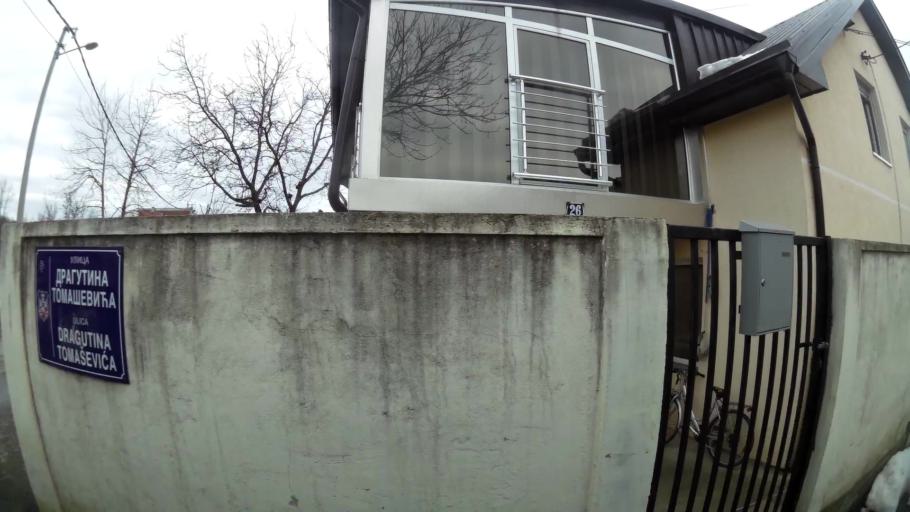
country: RS
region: Central Serbia
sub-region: Belgrade
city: Rakovica
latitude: 44.7439
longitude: 20.4000
